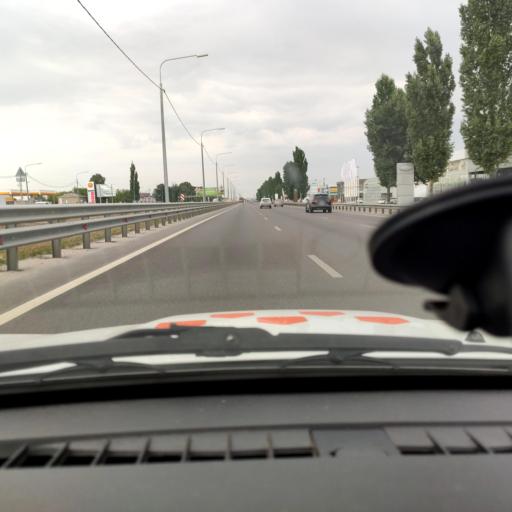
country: RU
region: Voronezj
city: Podgornoye
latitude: 51.7743
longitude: 39.1953
